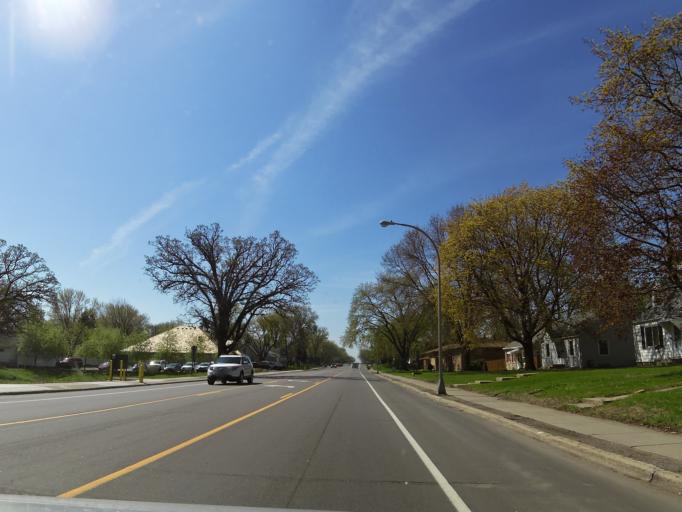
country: US
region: Minnesota
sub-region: Hennepin County
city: Richfield
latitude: 44.8776
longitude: -93.3086
